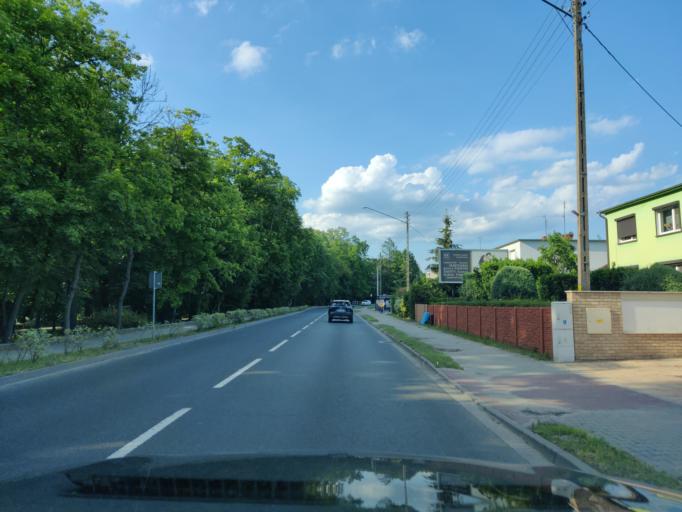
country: PL
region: Greater Poland Voivodeship
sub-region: Powiat wolsztynski
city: Wolsztyn
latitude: 52.1198
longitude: 16.1193
